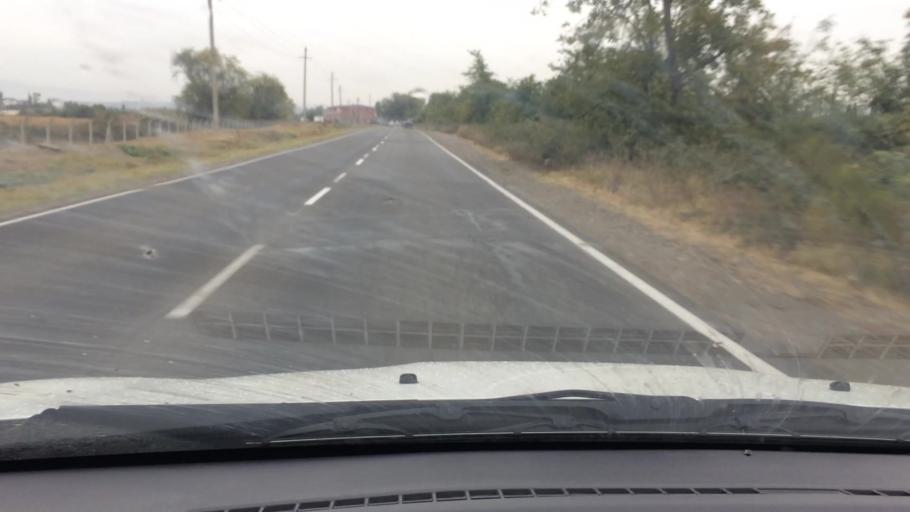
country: GE
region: Kvemo Kartli
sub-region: Marneuli
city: Marneuli
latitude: 41.4683
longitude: 44.8045
